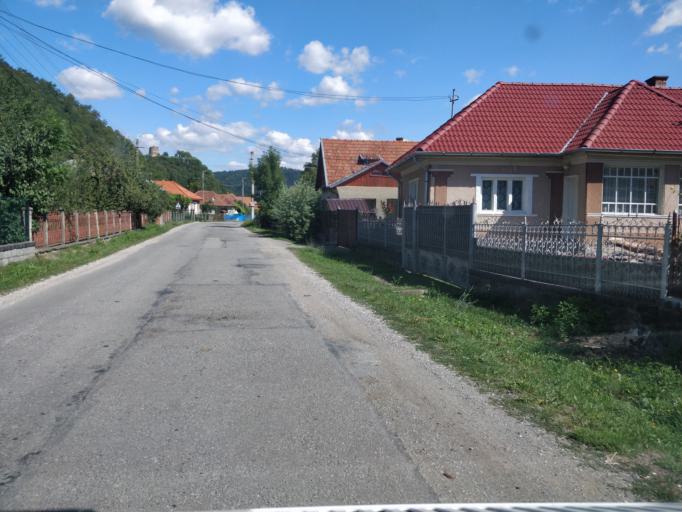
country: RO
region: Cluj
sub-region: Comuna Poeni
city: Poeni
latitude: 46.8746
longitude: 22.8794
